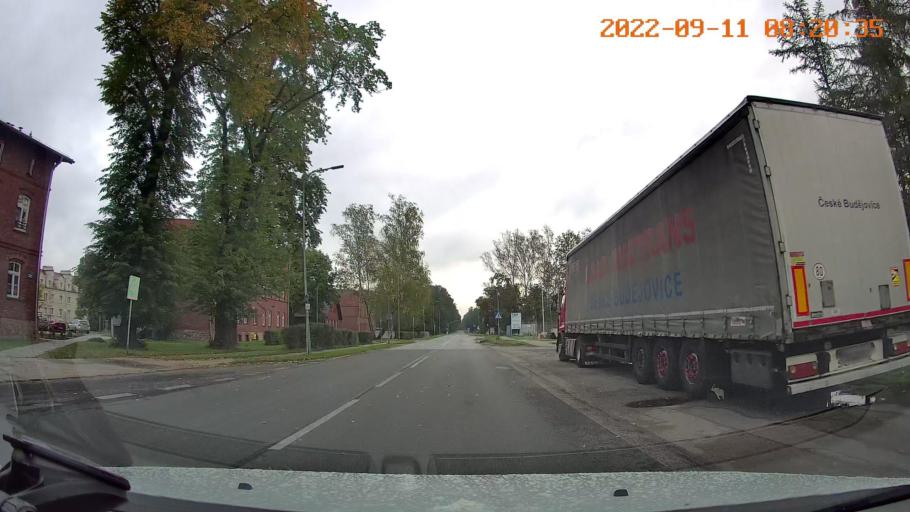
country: PL
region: Silesian Voivodeship
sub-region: Tychy
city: Tychy
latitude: 50.1599
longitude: 19.0109
